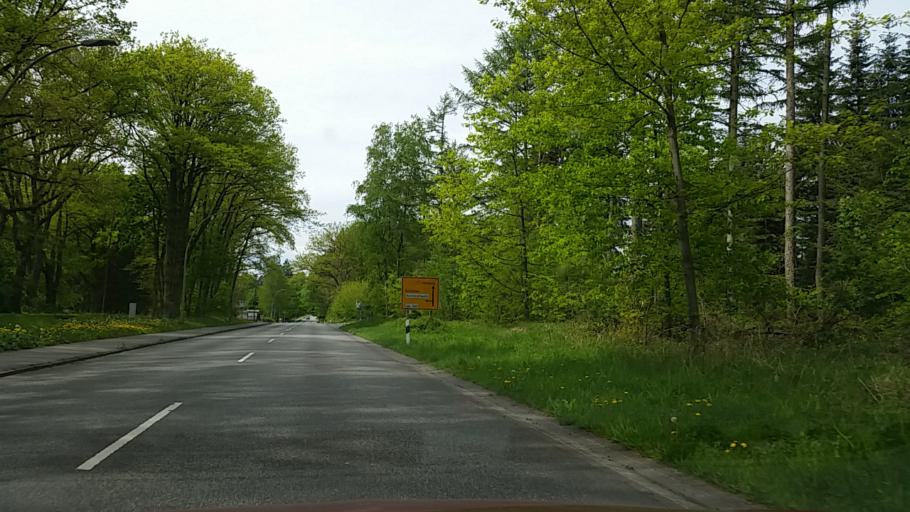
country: DE
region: Schleswig-Holstein
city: Hamwarde
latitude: 53.4240
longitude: 10.4197
